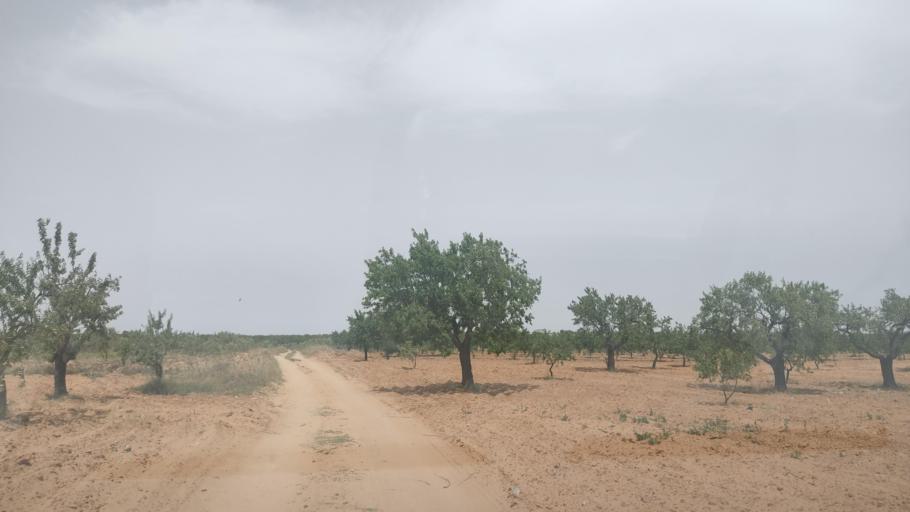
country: TN
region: Safaqis
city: Sfax
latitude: 34.8425
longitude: 10.5925
